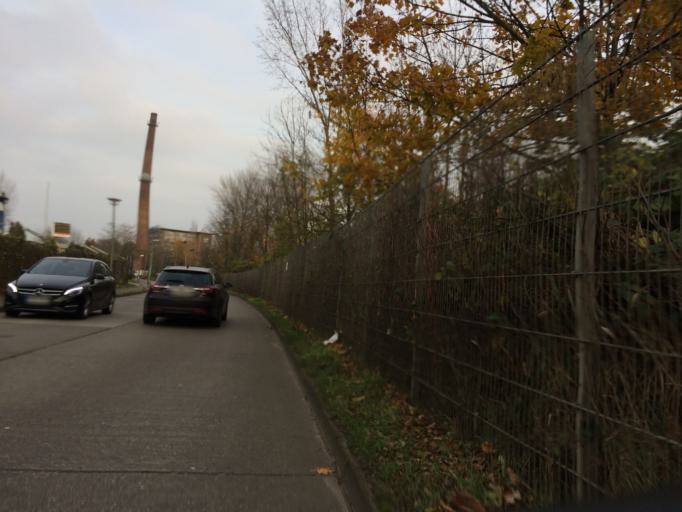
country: DE
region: Berlin
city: Rummelsburg
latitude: 52.5064
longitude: 13.4839
